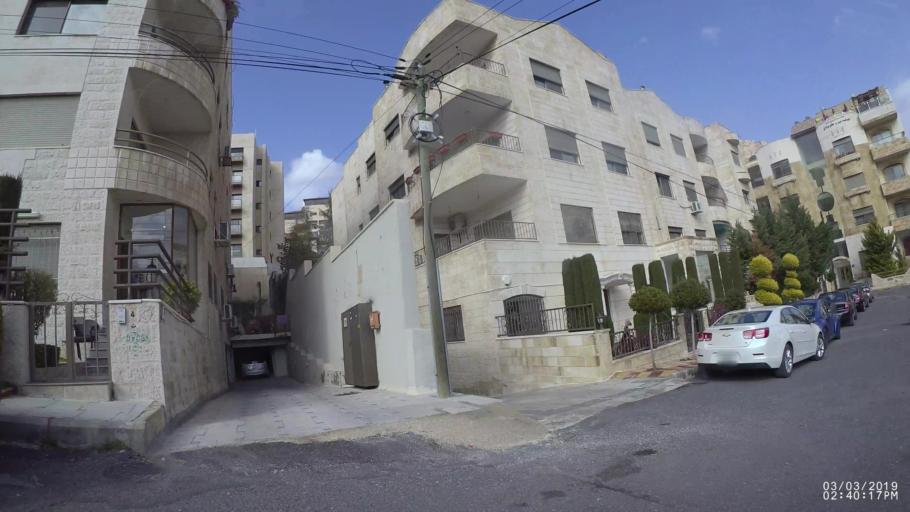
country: JO
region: Amman
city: Amman
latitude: 31.9612
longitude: 35.8946
